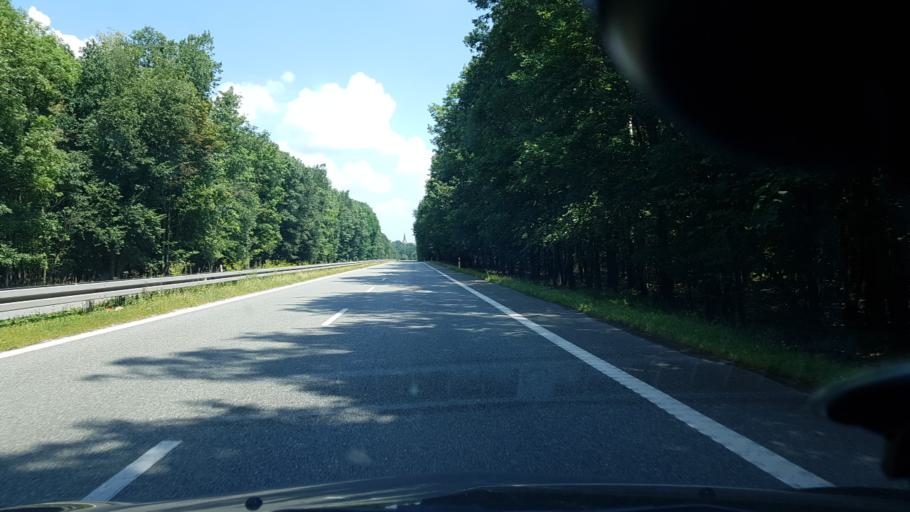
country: PL
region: Silesian Voivodeship
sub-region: Powiat pszczynski
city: Rudziczka
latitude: 50.0733
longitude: 18.7425
